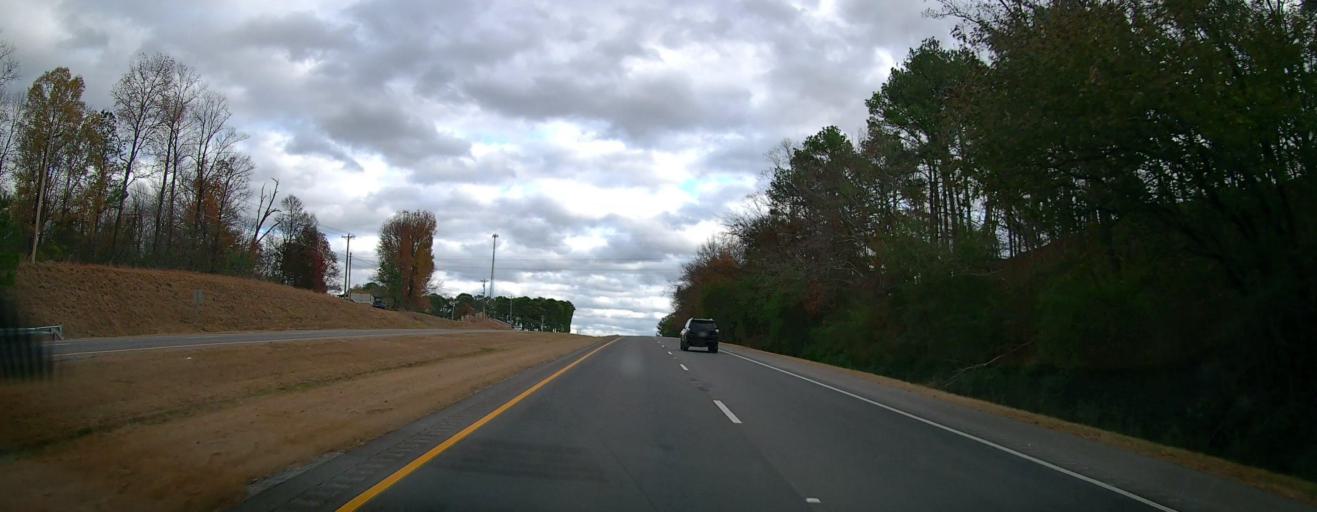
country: US
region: Alabama
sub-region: Cullman County
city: Cullman
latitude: 34.2305
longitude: -86.9130
